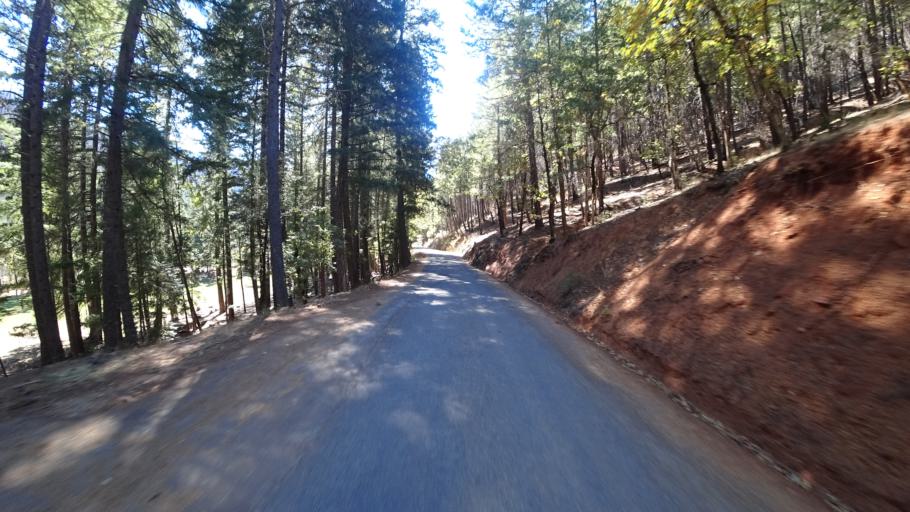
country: US
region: California
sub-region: Siskiyou County
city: Happy Camp
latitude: 41.3159
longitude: -123.0642
